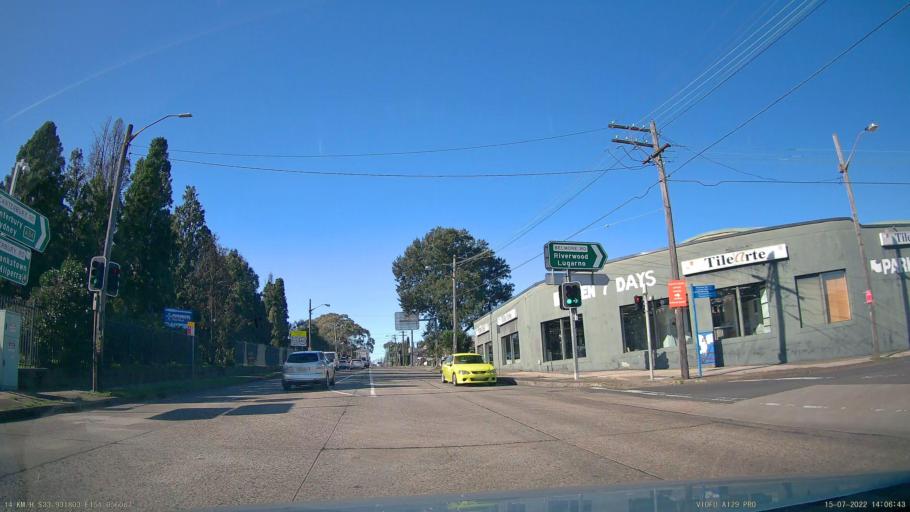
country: AU
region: New South Wales
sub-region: Canterbury
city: Roselands
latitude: -33.9316
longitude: 151.0561
